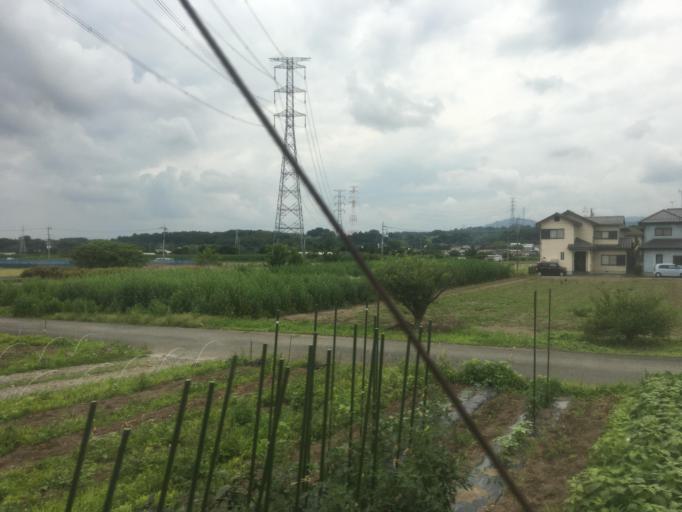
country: JP
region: Gunma
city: Yoshii
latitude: 36.2634
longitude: 139.0152
